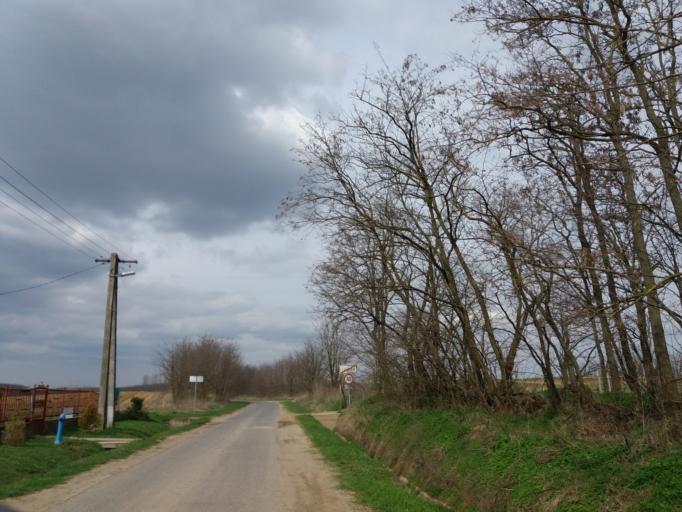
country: HU
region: Szabolcs-Szatmar-Bereg
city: Petnehaza
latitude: 48.0631
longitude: 22.0460
